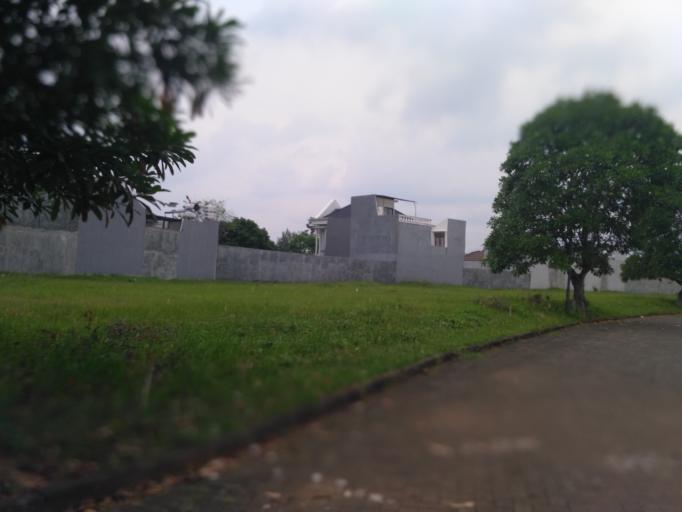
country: ID
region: Central Java
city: Semarang
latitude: -7.0625
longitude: 110.4311
